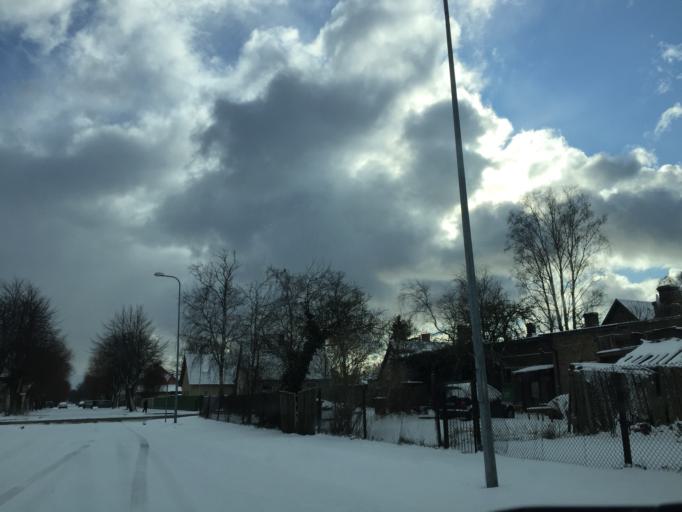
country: LV
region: Ventspils
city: Ventspils
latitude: 57.3850
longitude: 21.5629
